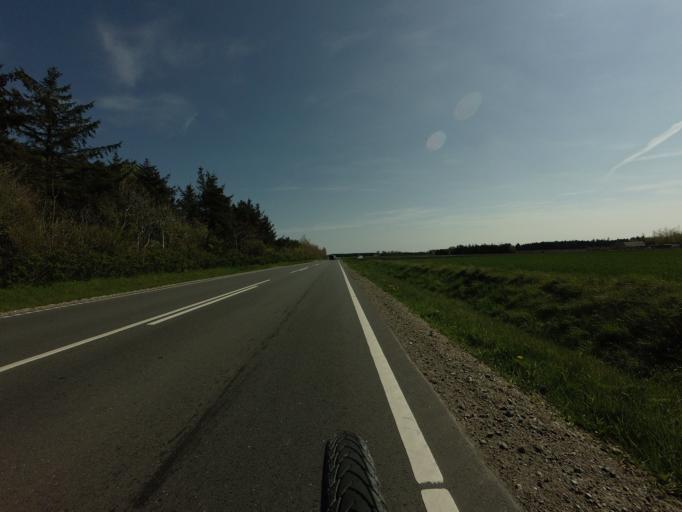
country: DK
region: North Denmark
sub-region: Jammerbugt Kommune
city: Pandrup
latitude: 57.2207
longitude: 9.6598
